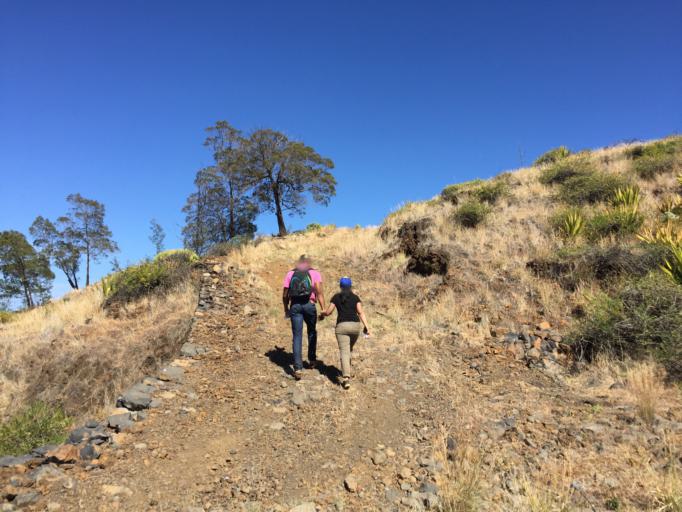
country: CV
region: Mosteiros
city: Porto dos Mosteiros
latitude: 15.0067
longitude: -24.3587
